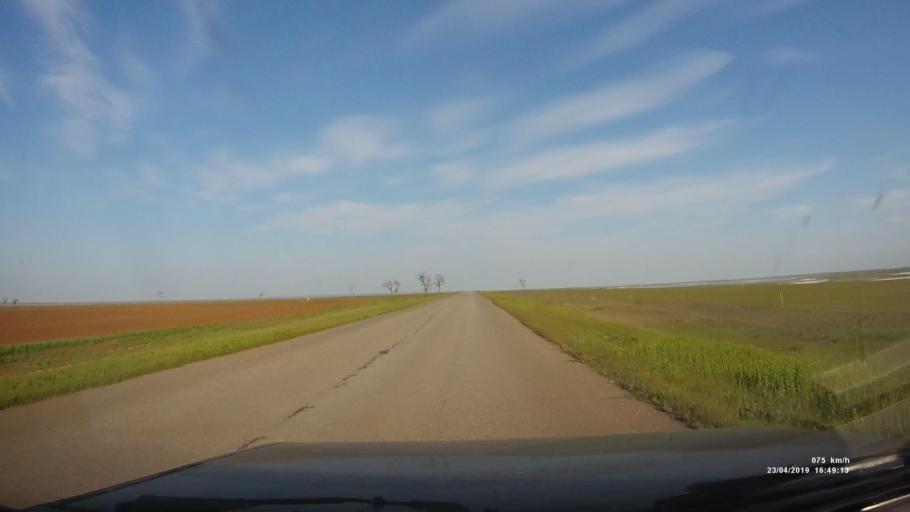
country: RU
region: Kalmykiya
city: Priyutnoye
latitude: 46.3319
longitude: 43.2731
